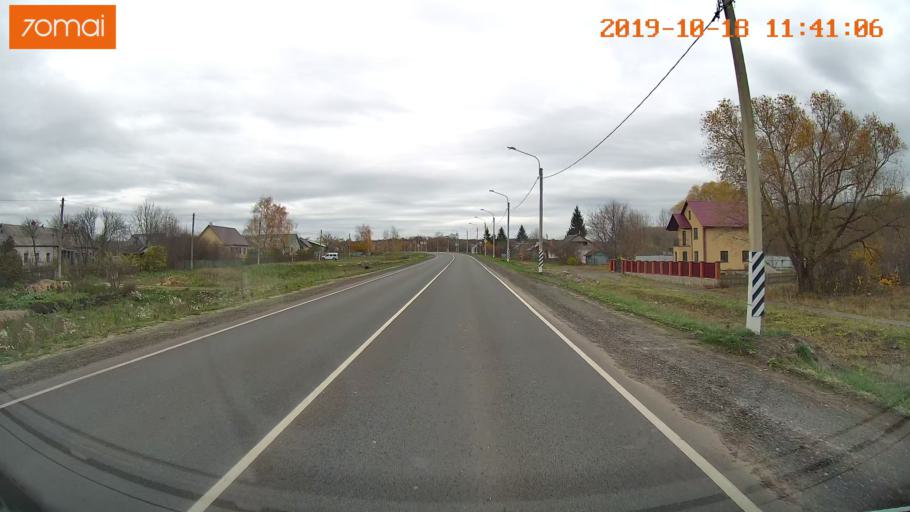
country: RU
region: Rjazan
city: Oktyabr'skiy
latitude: 54.1816
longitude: 38.9004
